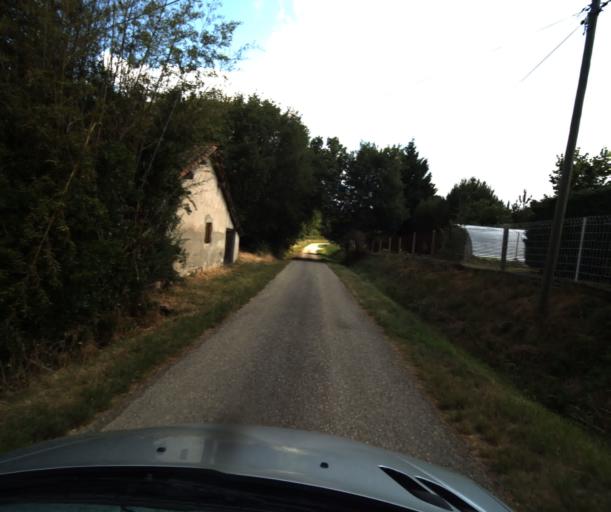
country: FR
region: Midi-Pyrenees
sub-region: Departement du Tarn-et-Garonne
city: Finhan
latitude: 43.9204
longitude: 1.2710
